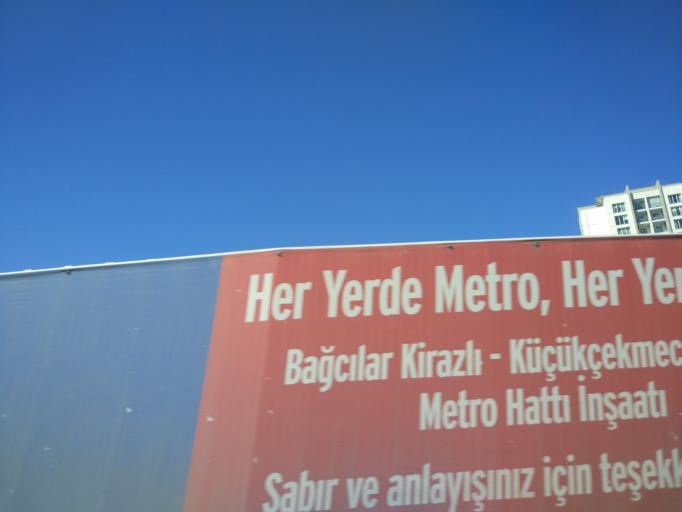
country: TR
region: Istanbul
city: Mahmutbey
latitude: 41.0335
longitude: 28.7805
